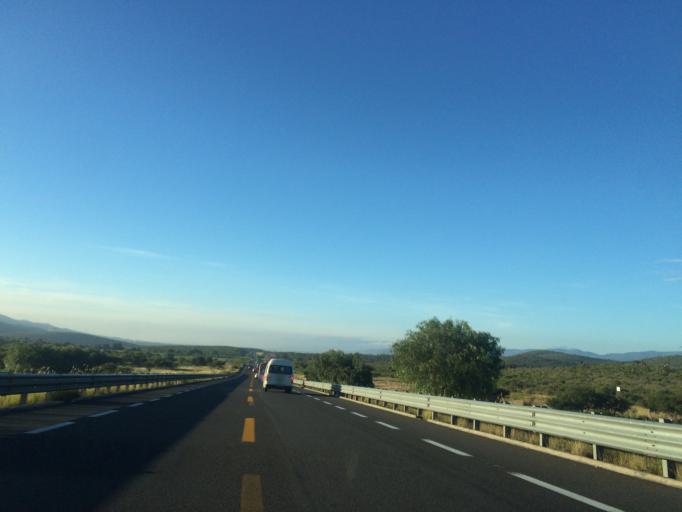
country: MX
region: Puebla
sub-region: Tehuacan
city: Magdalena Cuayucatepec
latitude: 18.5958
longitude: -97.4729
